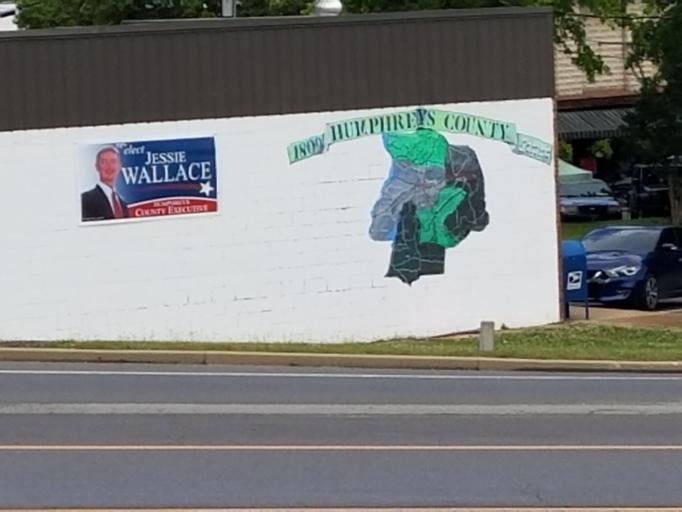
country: US
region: Tennessee
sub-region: Humphreys County
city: Waverly
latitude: 36.0817
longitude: -87.7939
